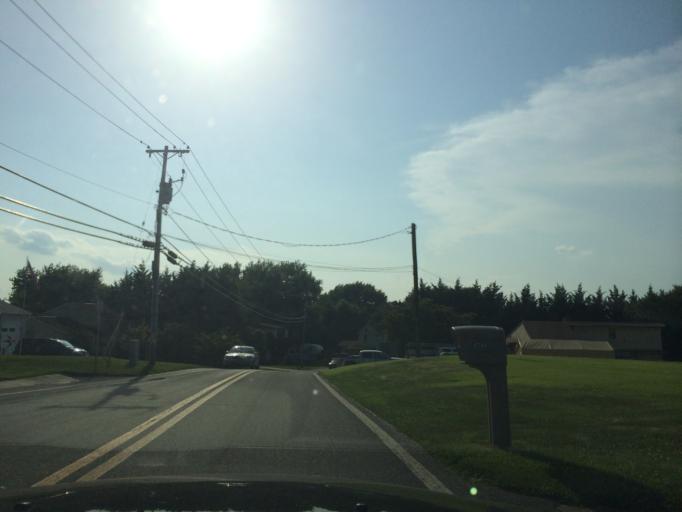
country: US
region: Maryland
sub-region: Carroll County
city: Eldersburg
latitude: 39.4182
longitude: -76.9605
